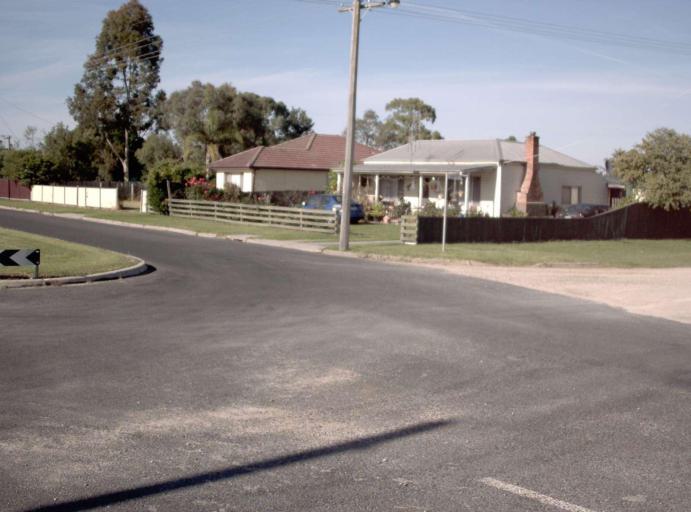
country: AU
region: Victoria
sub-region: East Gippsland
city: Lakes Entrance
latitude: -37.6920
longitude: 148.4586
